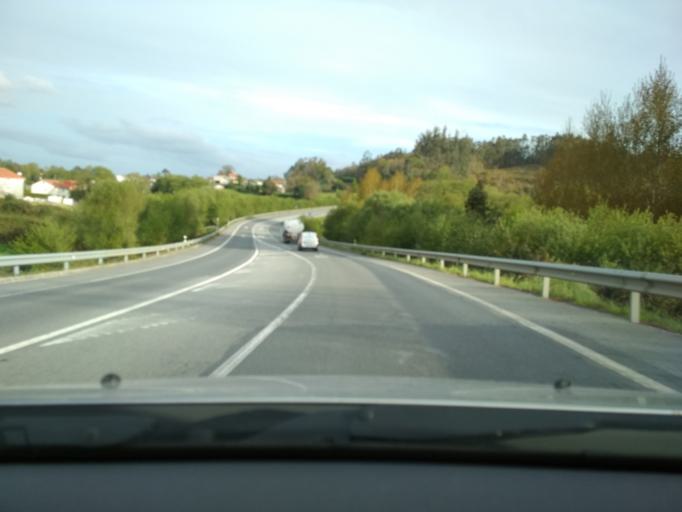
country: ES
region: Galicia
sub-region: Provincia da Coruna
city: Cerceda
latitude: 43.2193
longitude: -8.4577
